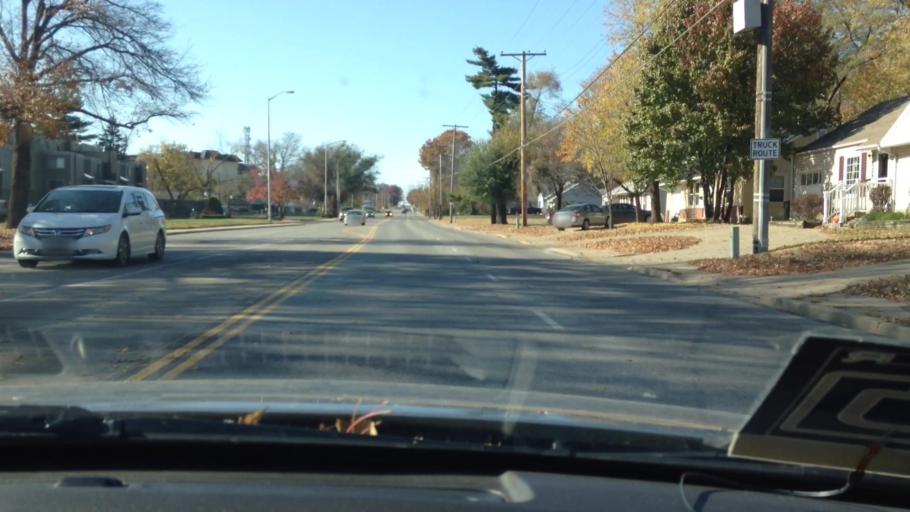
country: US
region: Kansas
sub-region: Johnson County
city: Overland Park
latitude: 38.9931
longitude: -94.6586
